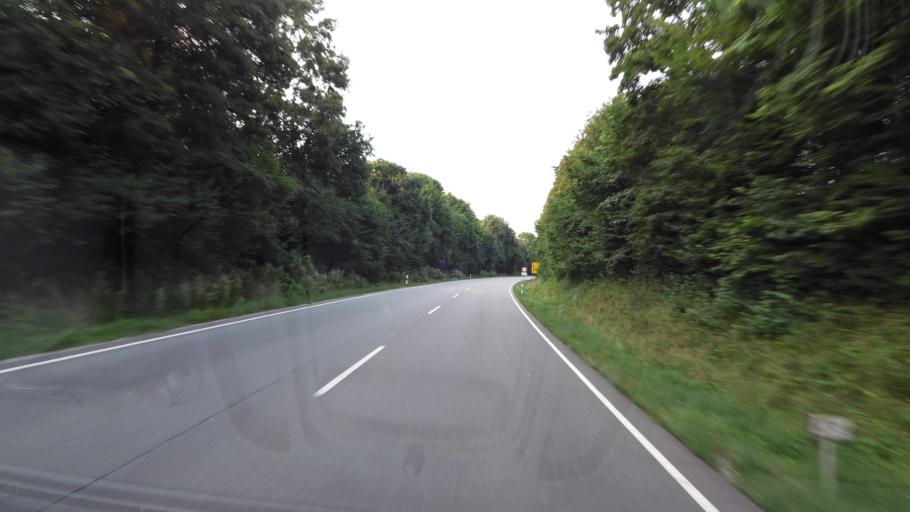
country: DE
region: Bavaria
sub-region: Lower Bavaria
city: Simbach am Inn
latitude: 48.2687
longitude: 13.0145
